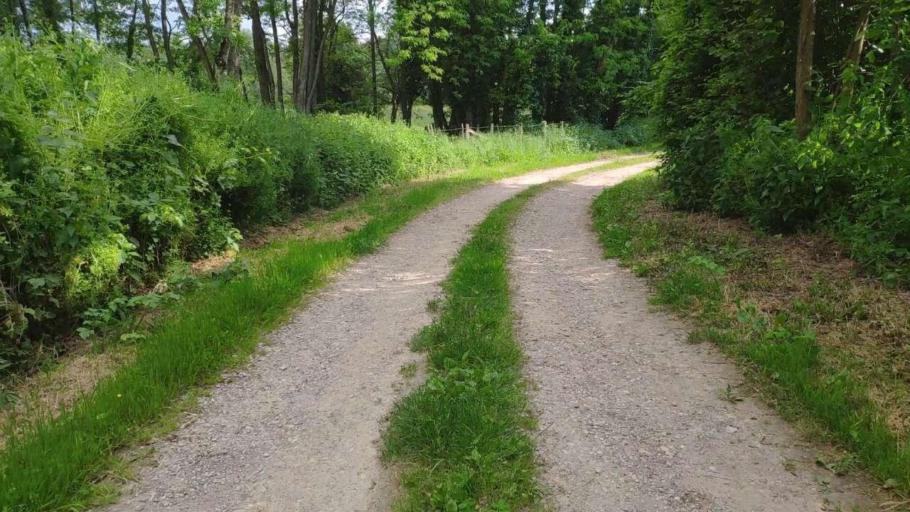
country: FR
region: Franche-Comte
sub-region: Departement du Jura
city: Bletterans
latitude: 46.8110
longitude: 5.3528
